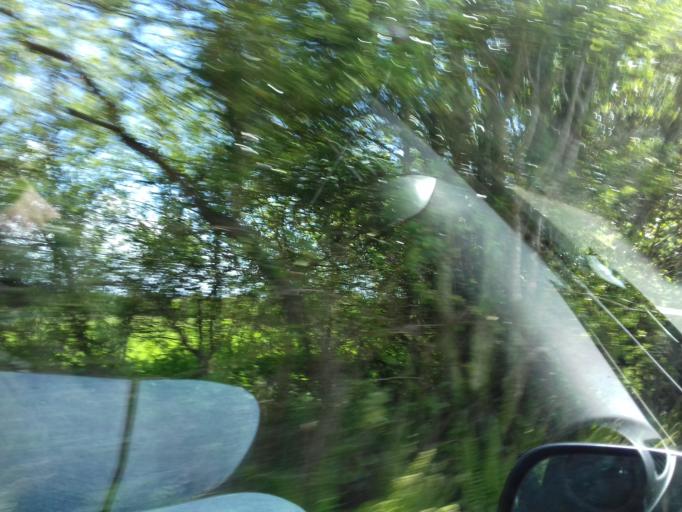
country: IE
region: Munster
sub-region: Waterford
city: Dunmore East
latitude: 52.2447
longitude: -6.8606
